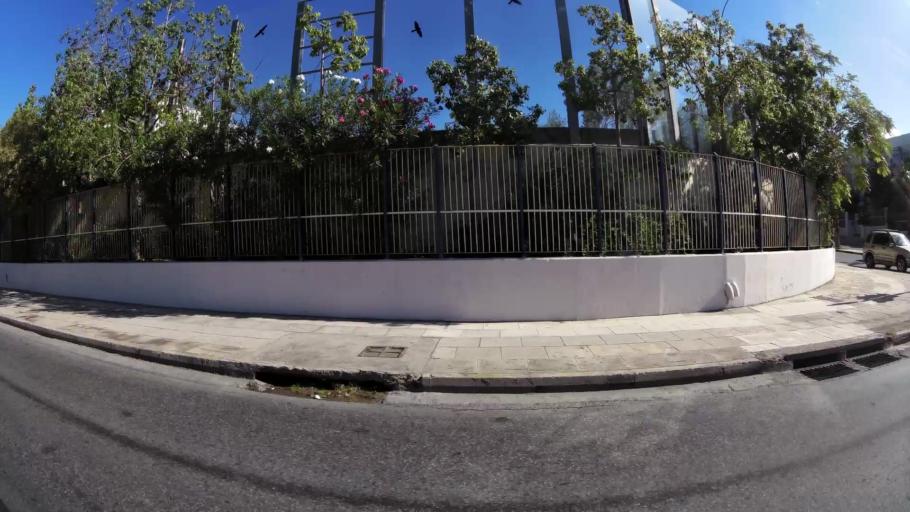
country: GR
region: Attica
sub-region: Nomarchia Athinas
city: Glyfada
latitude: 37.8613
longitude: 23.7631
